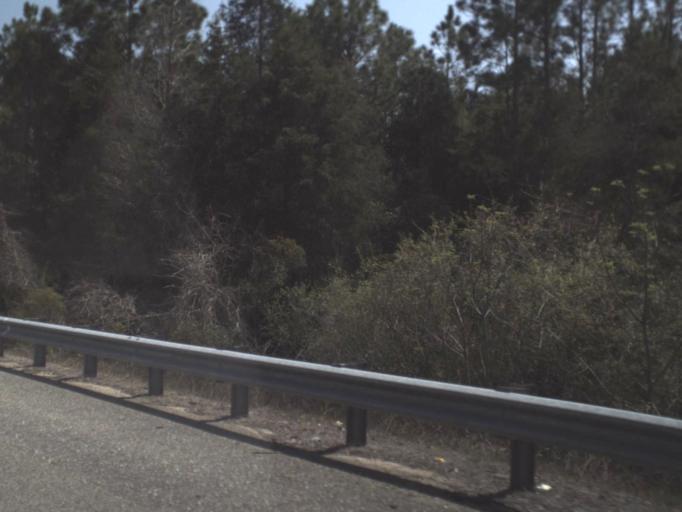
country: US
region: Florida
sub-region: Gulf County
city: Port Saint Joe
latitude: 29.7492
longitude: -85.2428
